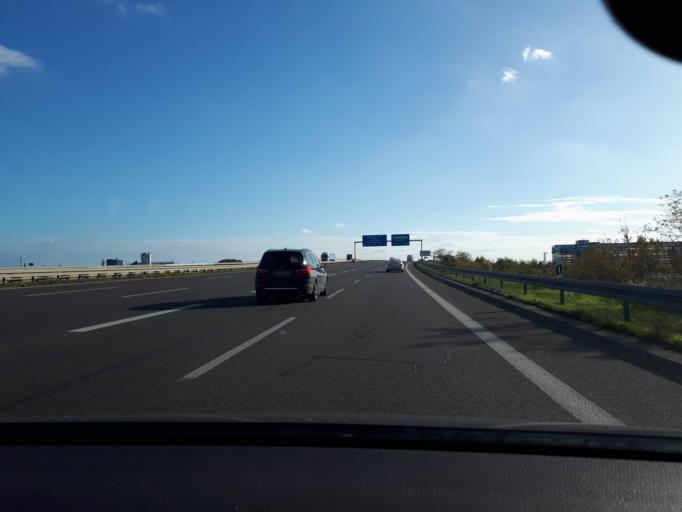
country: DE
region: Brandenburg
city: Schonefeld
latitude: 52.3809
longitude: 13.5402
